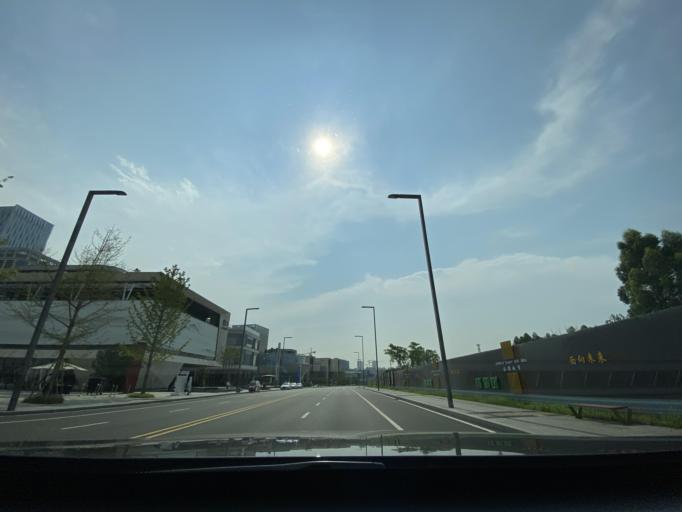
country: CN
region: Sichuan
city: Dongsheng
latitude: 30.3926
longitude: 104.0854
